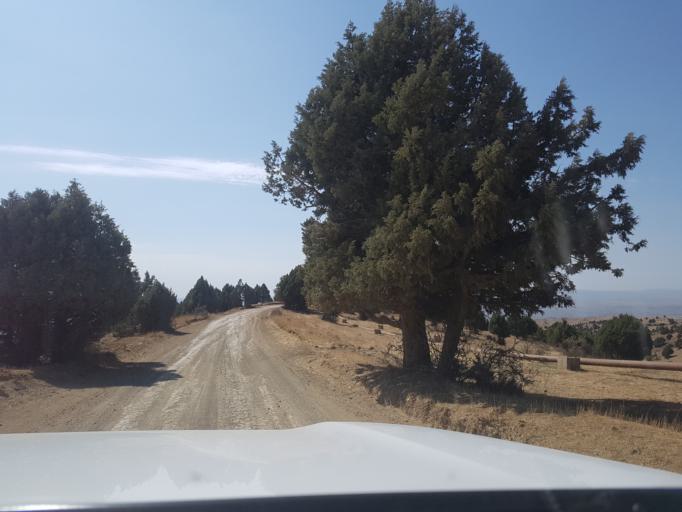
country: TM
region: Ahal
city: Baharly
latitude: 38.3179
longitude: 56.9543
